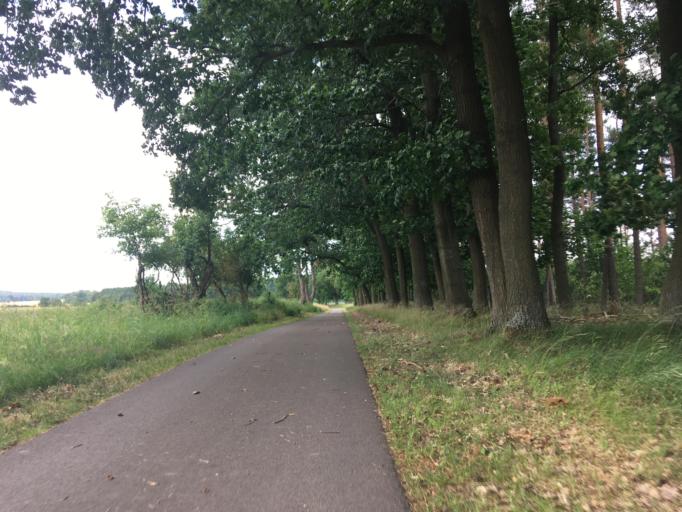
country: DE
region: Brandenburg
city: Althuttendorf
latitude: 53.0245
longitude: 13.8566
